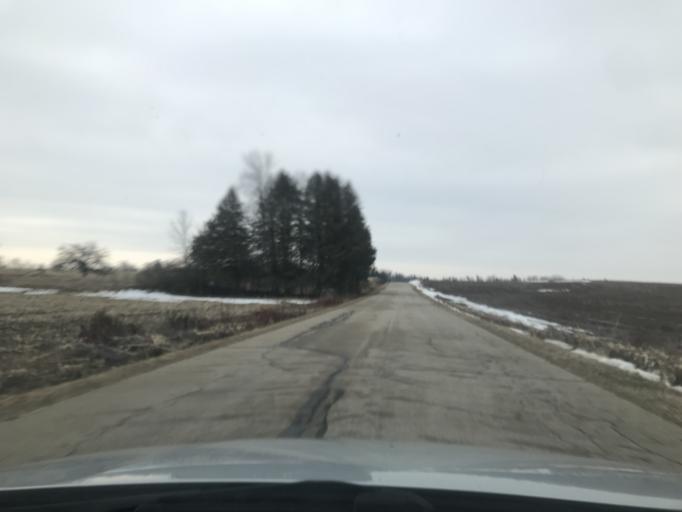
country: US
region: Wisconsin
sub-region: Marinette County
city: Peshtigo
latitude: 45.1150
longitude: -88.0082
